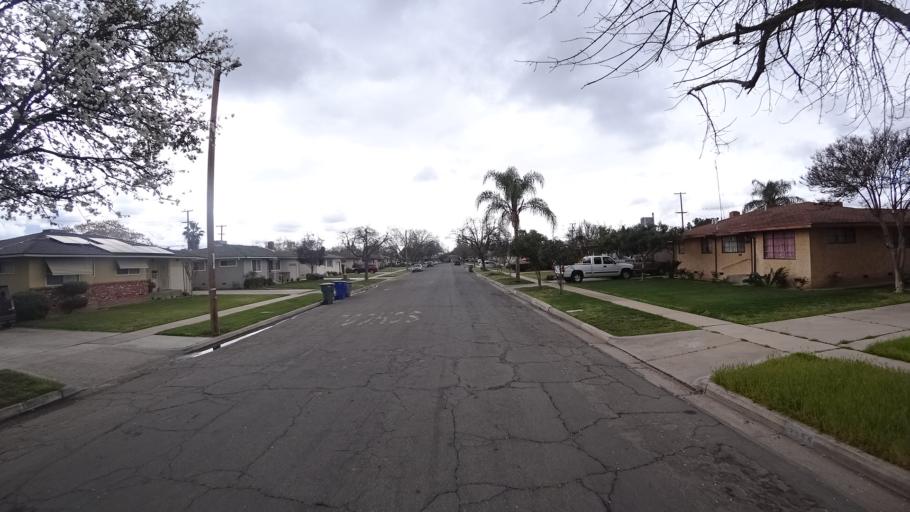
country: US
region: California
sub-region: Fresno County
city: Fresno
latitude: 36.7895
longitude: -119.8375
